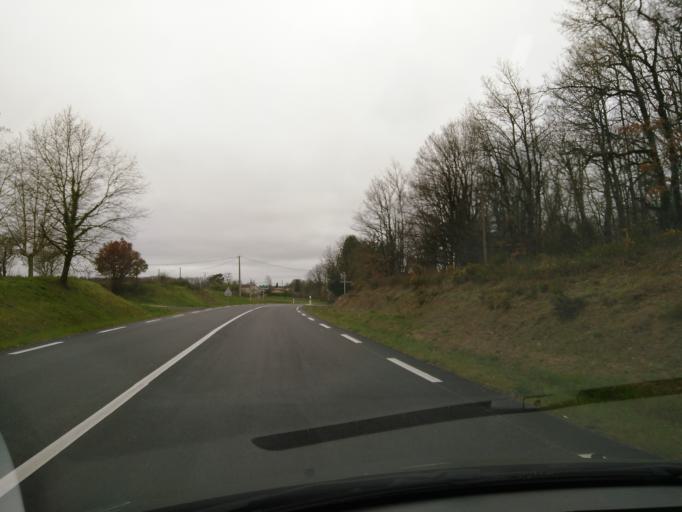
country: FR
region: Aquitaine
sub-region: Departement de la Dordogne
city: Monbazillac
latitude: 44.7352
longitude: 0.5447
